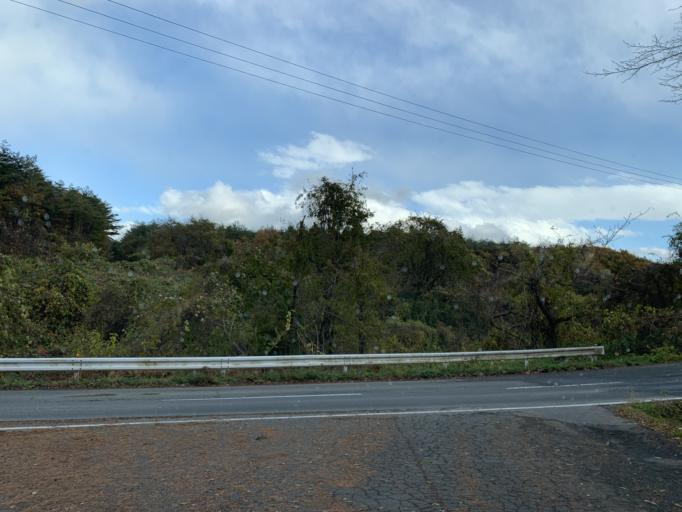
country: JP
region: Iwate
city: Mizusawa
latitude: 39.0451
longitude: 141.0759
